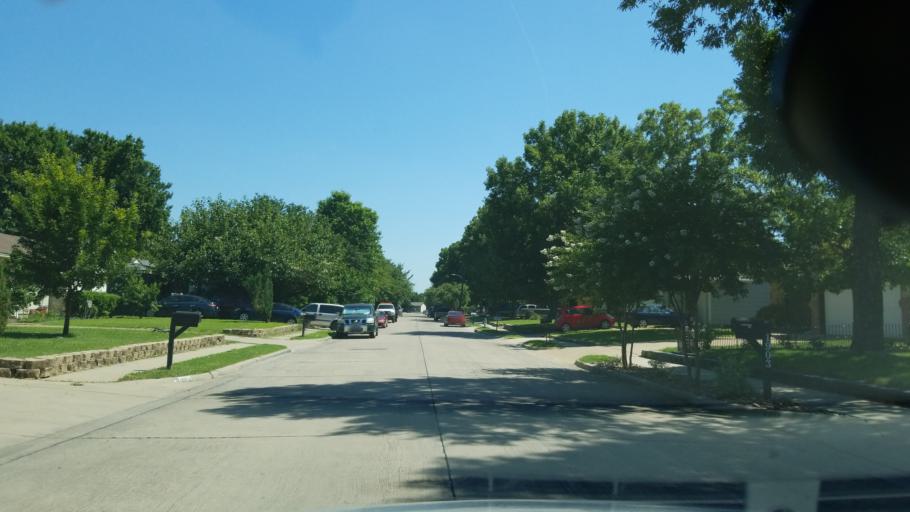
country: US
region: Texas
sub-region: Dallas County
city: Irving
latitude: 32.8341
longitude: -96.9365
